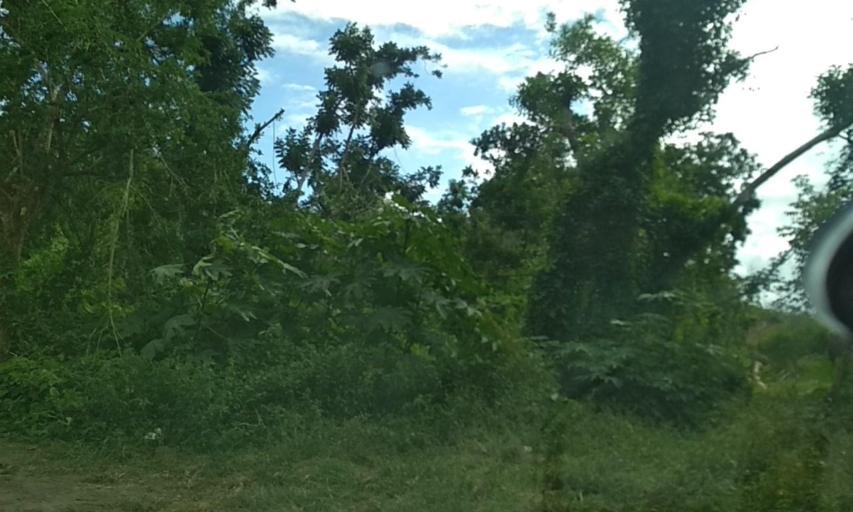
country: MX
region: Veracruz
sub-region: Papantla
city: Residencial Tajin
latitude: 20.6399
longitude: -97.3633
